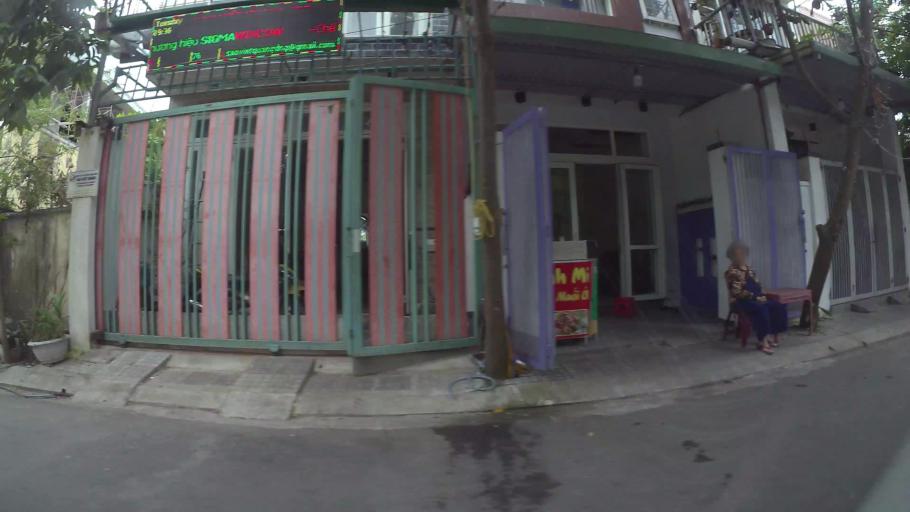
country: VN
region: Da Nang
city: Thanh Khe
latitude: 16.0690
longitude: 108.1846
